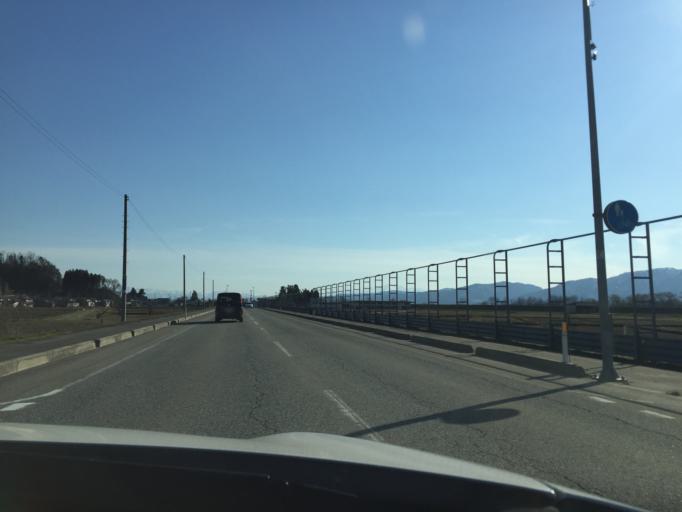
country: JP
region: Yamagata
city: Nagai
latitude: 38.1428
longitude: 140.0595
